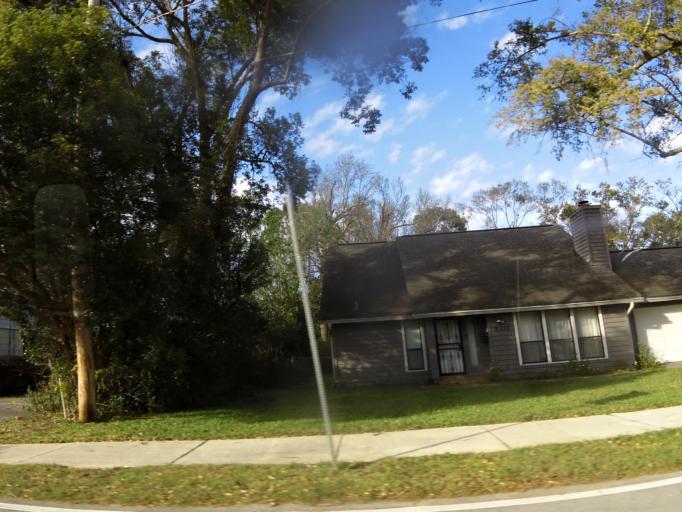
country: US
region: Florida
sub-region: Duval County
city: Jacksonville
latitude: 30.2860
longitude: -81.6113
